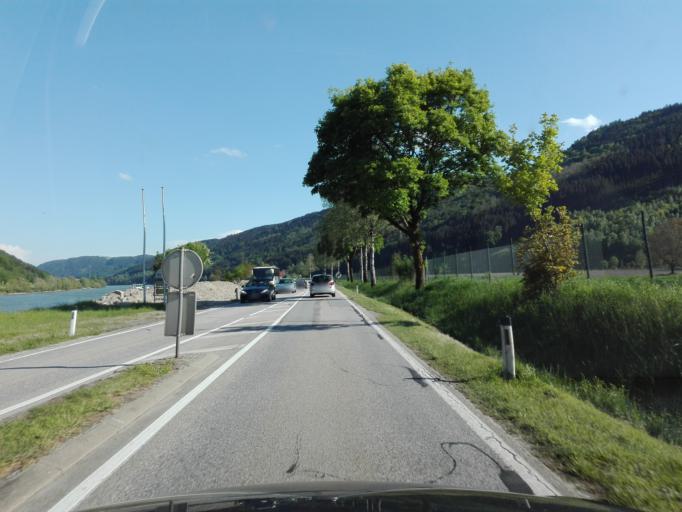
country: AT
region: Upper Austria
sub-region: Politischer Bezirk Rohrbach
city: Pfarrkirchen im Muehlkreis
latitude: 48.5010
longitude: 13.7364
